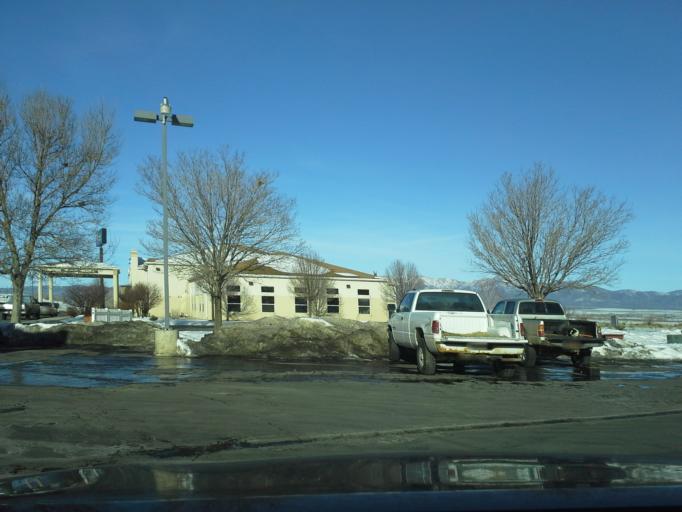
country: US
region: Utah
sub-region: Beaver County
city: Beaver
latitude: 38.2510
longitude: -112.6474
